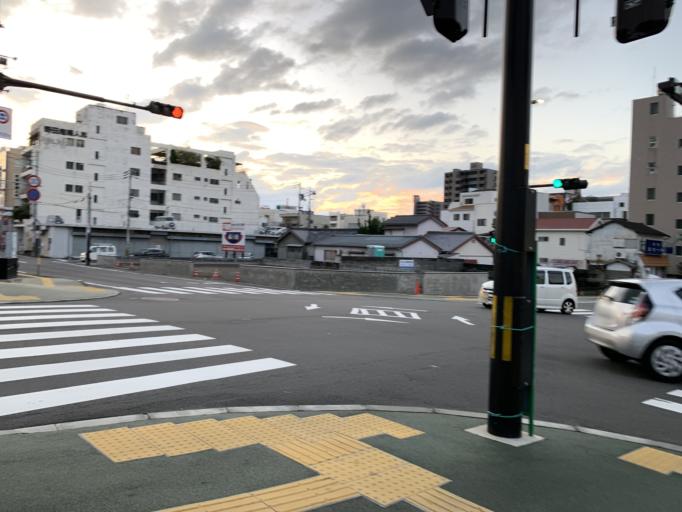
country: JP
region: Tokushima
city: Tokushima-shi
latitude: 34.0672
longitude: 134.5537
